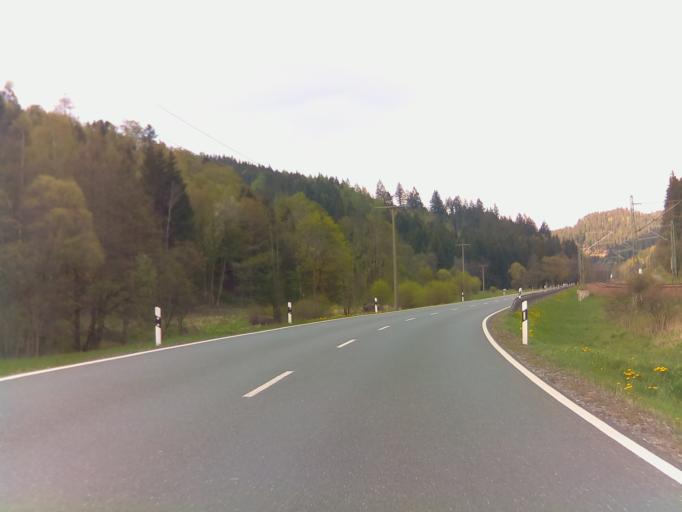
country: DE
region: Bavaria
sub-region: Upper Franconia
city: Pressig
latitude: 50.3723
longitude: 11.3299
